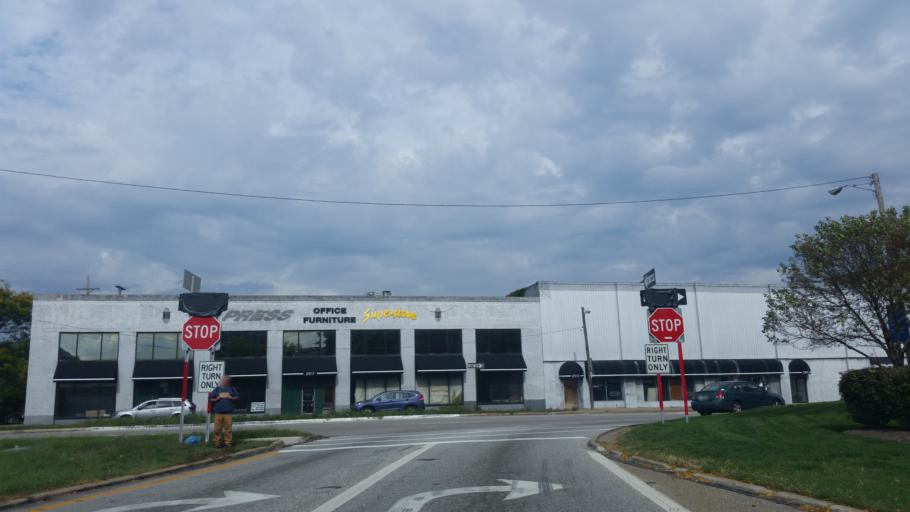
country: US
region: Ohio
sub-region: Cuyahoga County
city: Cleveland
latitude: 41.5041
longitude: -81.6686
